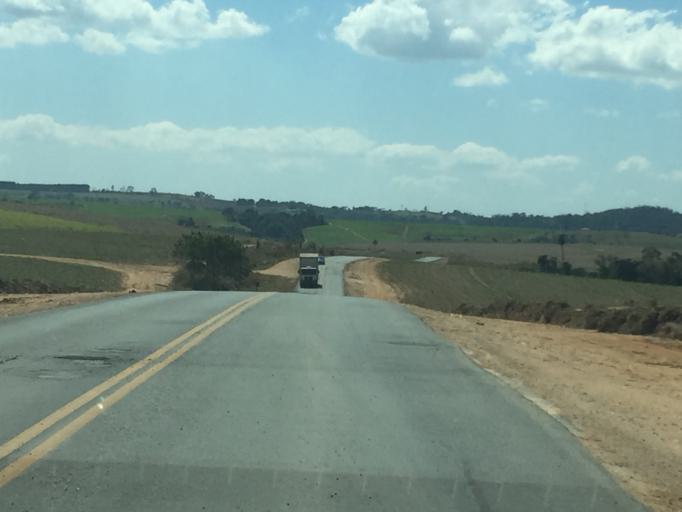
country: BR
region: Sao Paulo
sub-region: Moji-Guacu
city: Mogi-Gaucu
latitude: -22.3711
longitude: -46.8750
